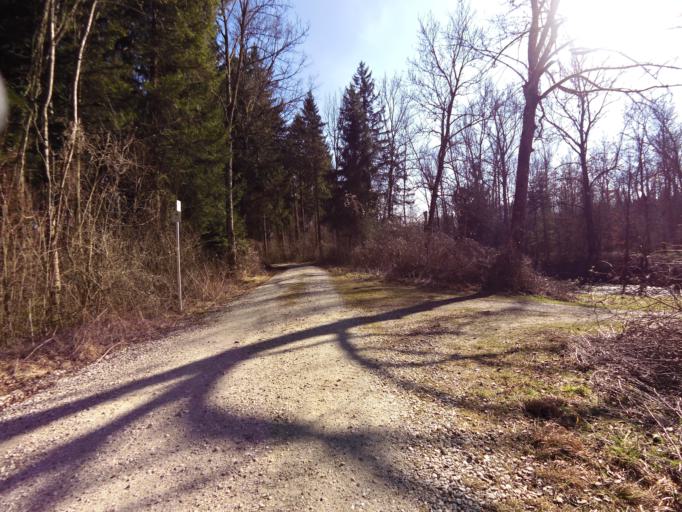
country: DE
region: Bavaria
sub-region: Upper Bavaria
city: Wang
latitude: 48.5006
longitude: 11.9812
